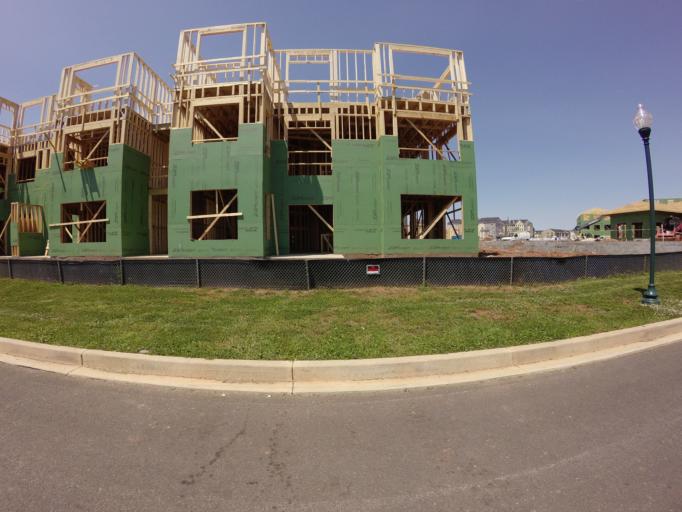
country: US
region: Maryland
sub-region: Frederick County
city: Ballenger Creek
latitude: 39.3924
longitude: -77.4540
